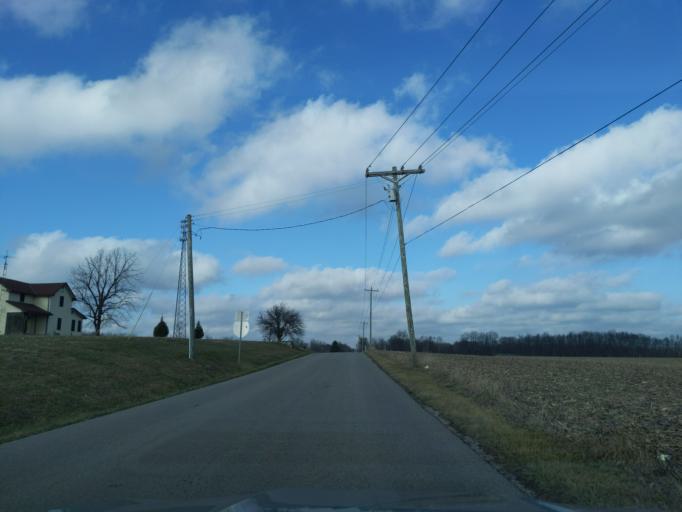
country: US
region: Indiana
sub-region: Ripley County
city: Batesville
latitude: 39.3194
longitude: -85.3258
